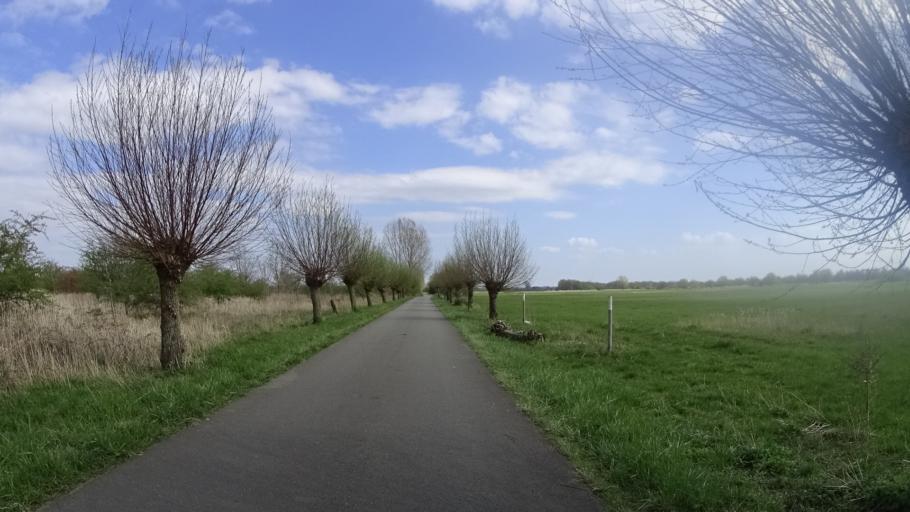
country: DE
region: Lower Saxony
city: Rhede
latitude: 53.0577
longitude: 7.2931
